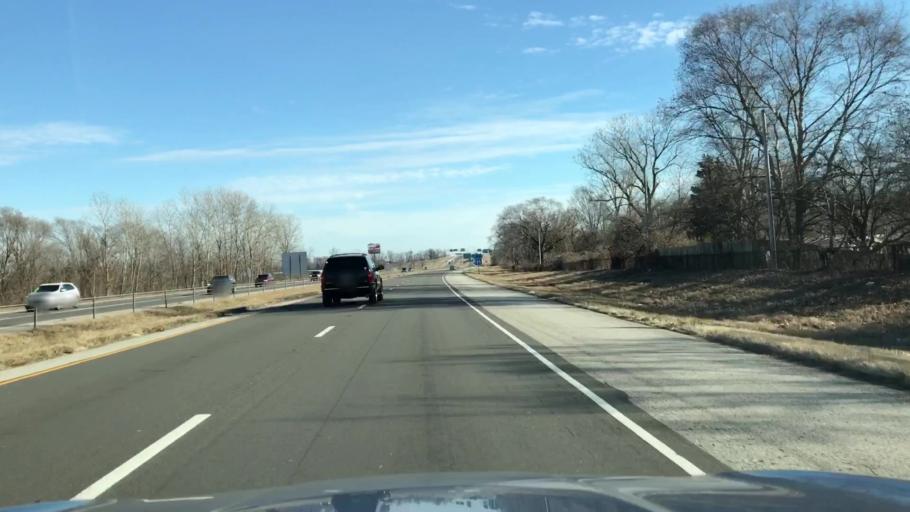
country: US
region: Illinois
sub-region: Madison County
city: Mitchell
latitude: 38.7641
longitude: -90.1073
